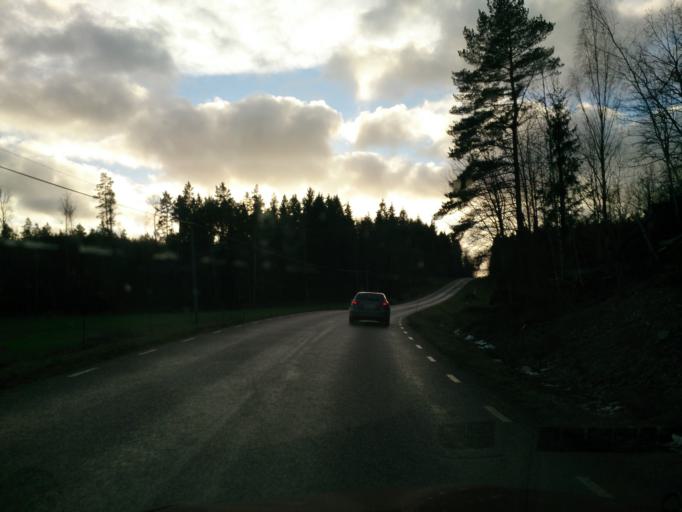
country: SE
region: OEstergoetland
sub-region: Atvidabergs Kommun
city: Atvidaberg
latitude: 58.3053
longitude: 16.0202
